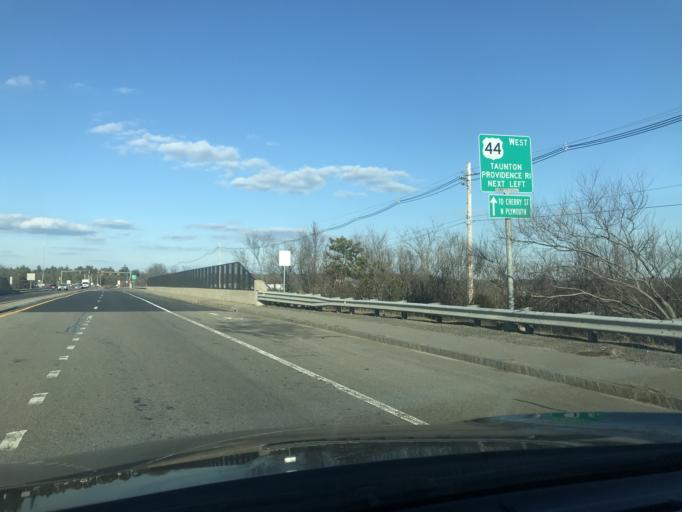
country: US
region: Massachusetts
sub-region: Plymouth County
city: North Plymouth
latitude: 41.9588
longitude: -70.7102
